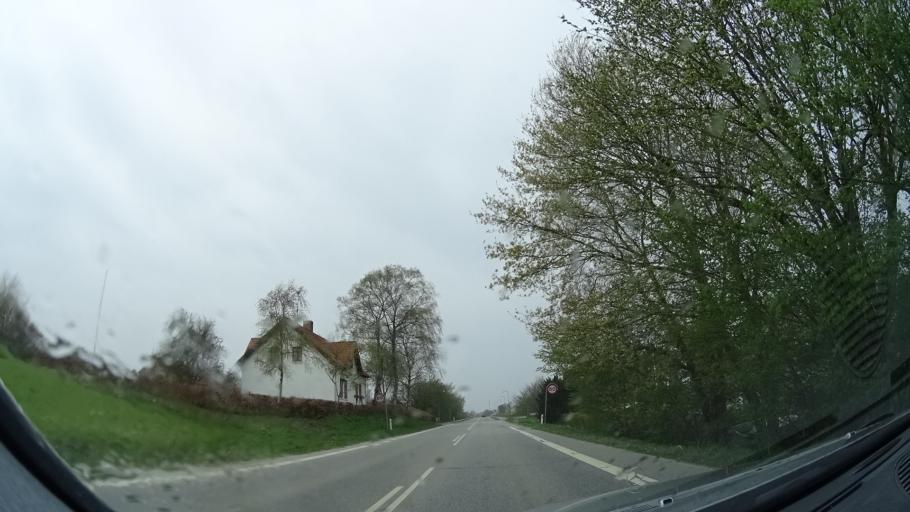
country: DK
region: Zealand
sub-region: Holbaek Kommune
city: Vipperod
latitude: 55.7061
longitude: 11.7664
